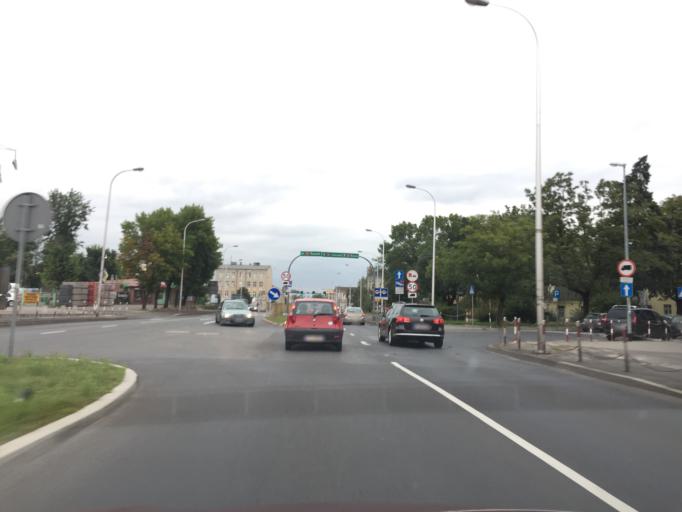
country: PL
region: Greater Poland Voivodeship
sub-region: Kalisz
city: Kalisz
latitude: 51.7582
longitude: 18.0757
